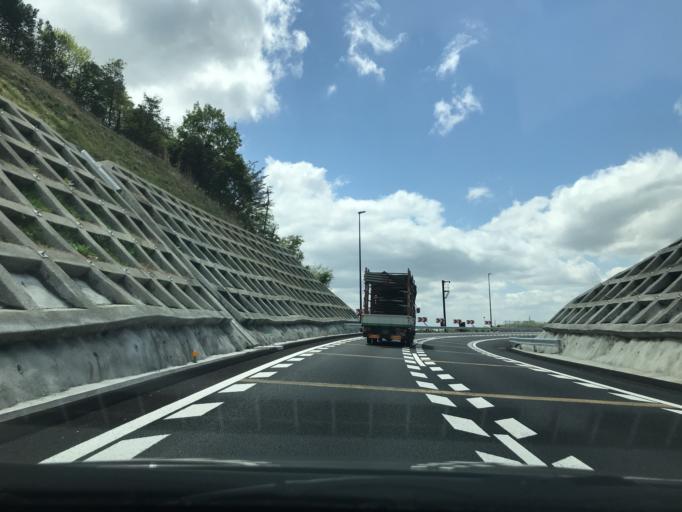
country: JP
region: Osaka
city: Takatsuki
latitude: 34.8843
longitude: 135.6226
